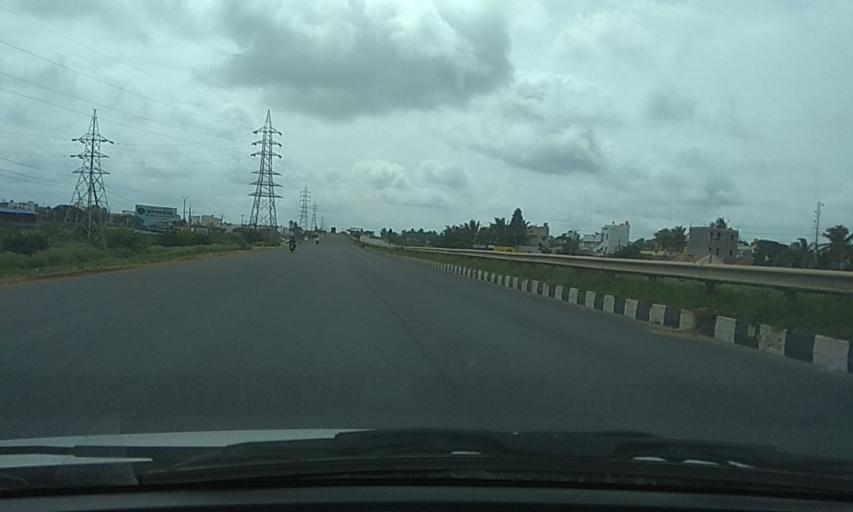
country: IN
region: Karnataka
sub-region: Davanagere
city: Harihar
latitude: 14.4433
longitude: 75.8947
